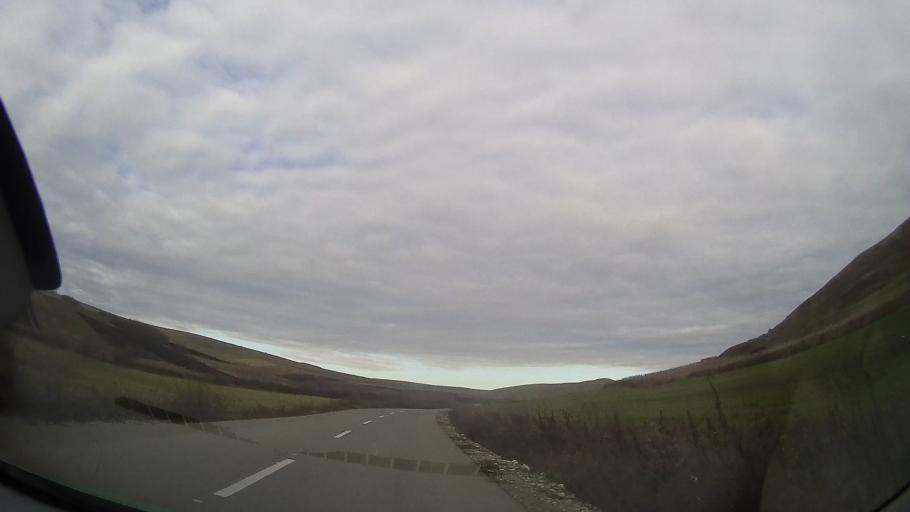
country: RO
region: Bistrita-Nasaud
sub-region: Comuna Silvasu de Campie
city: Silvasu de Campie
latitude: 46.7960
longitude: 24.2960
